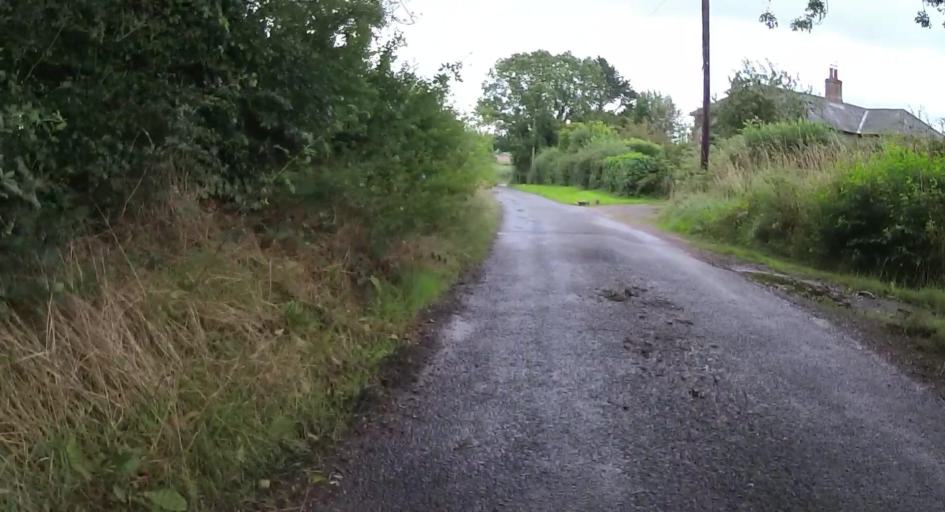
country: GB
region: England
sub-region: Hampshire
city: Andover
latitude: 51.2389
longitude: -1.4171
